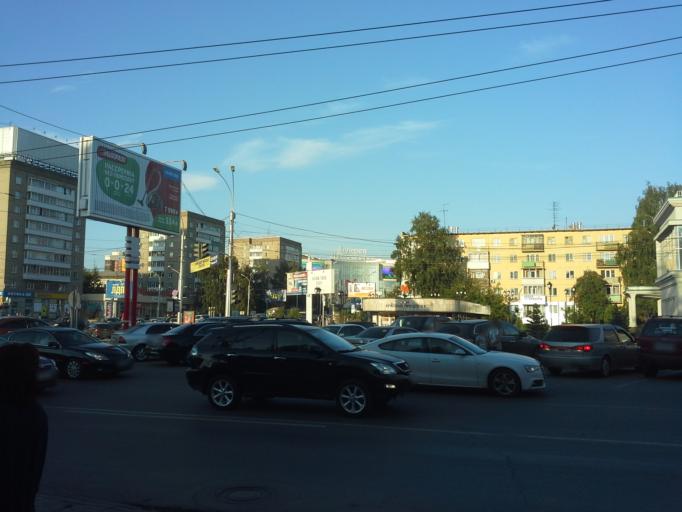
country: RU
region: Novosibirsk
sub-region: Novosibirskiy Rayon
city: Novosibirsk
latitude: 55.0416
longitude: 82.9168
